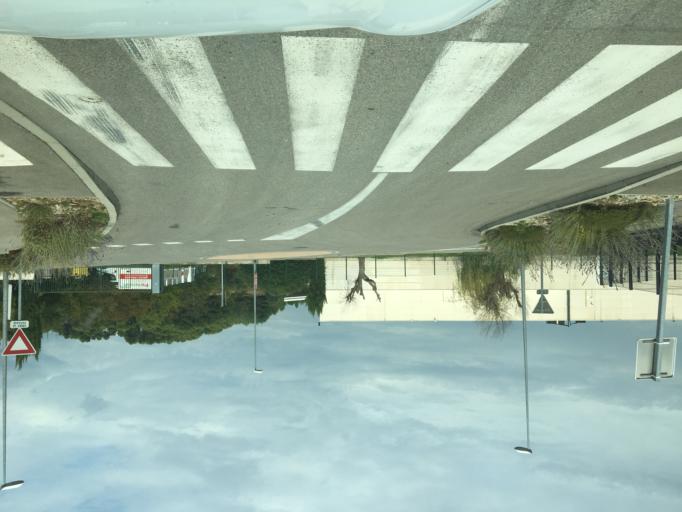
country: FR
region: Provence-Alpes-Cote d'Azur
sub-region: Departement des Bouches-du-Rhone
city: Bouc-Bel-Air
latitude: 43.4870
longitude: 5.3874
